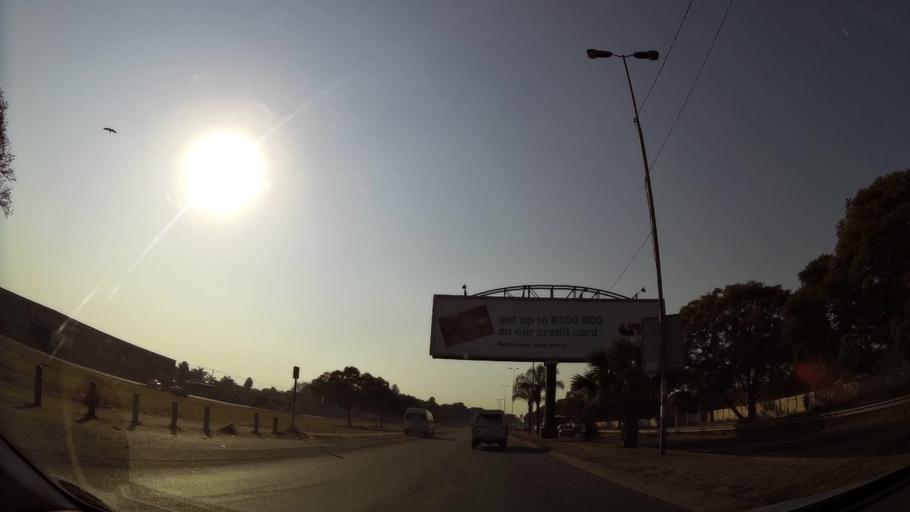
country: ZA
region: Gauteng
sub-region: City of Tshwane Metropolitan Municipality
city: Pretoria
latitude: -25.7112
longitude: 28.2707
